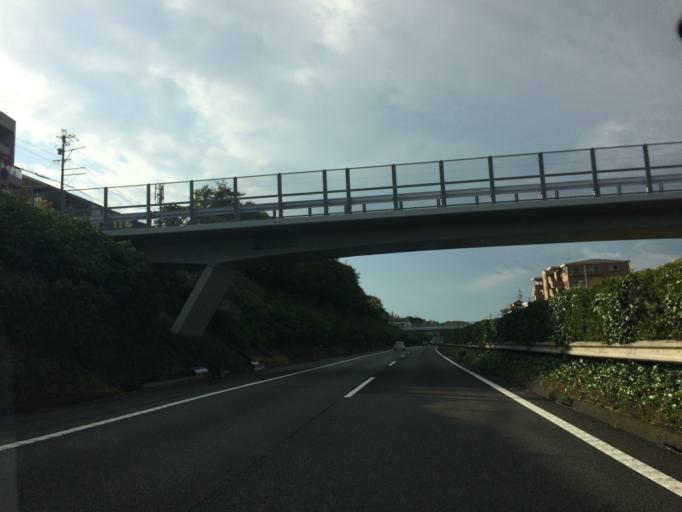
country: JP
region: Shizuoka
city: Shizuoka-shi
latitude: 34.9730
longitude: 138.4306
